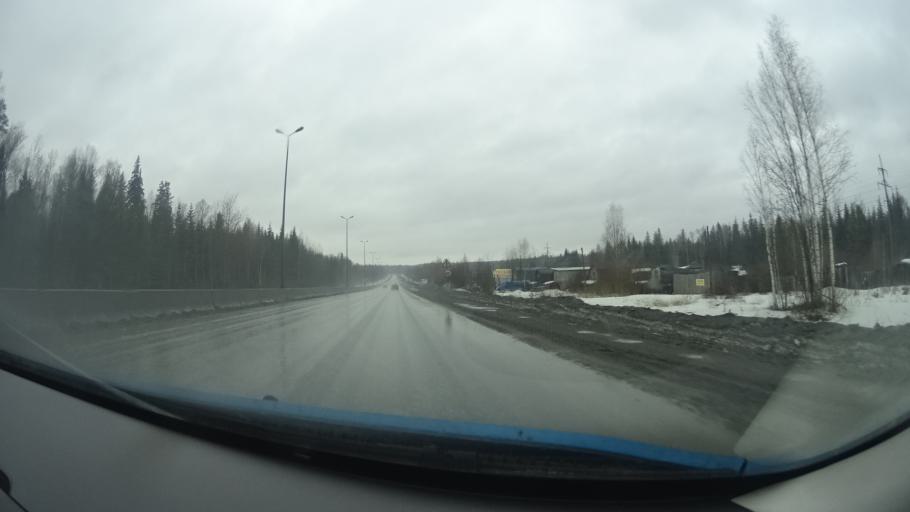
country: RU
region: Perm
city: Kondratovo
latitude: 58.0563
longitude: 56.1043
